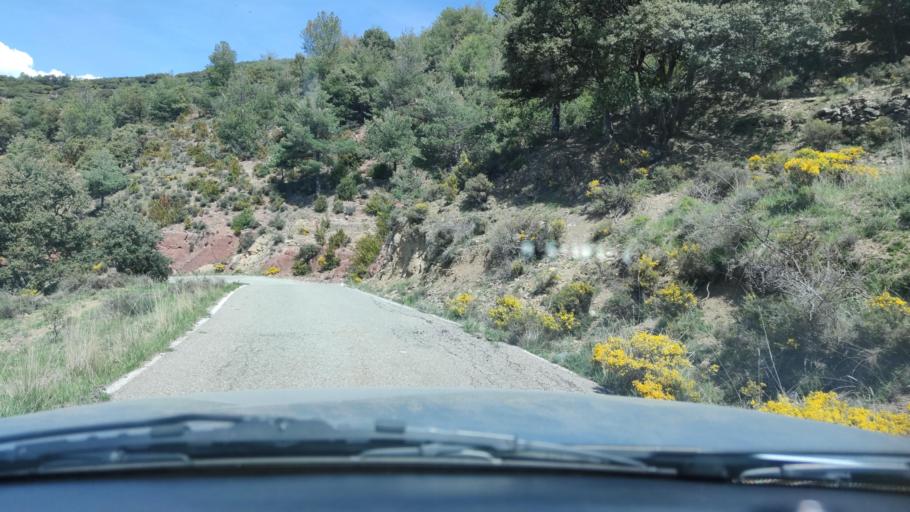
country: ES
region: Catalonia
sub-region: Provincia de Lleida
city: Sort
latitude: 42.3066
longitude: 1.1216
